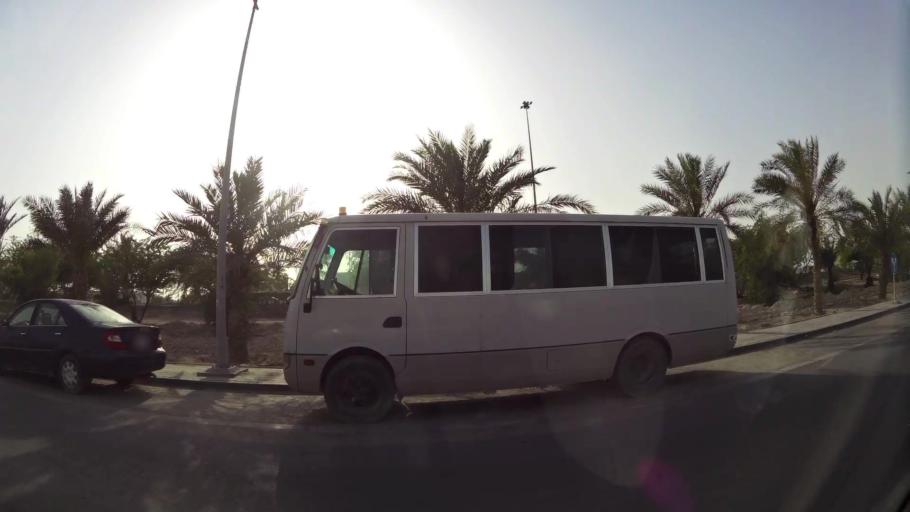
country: QA
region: Baladiyat ar Rayyan
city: Ar Rayyan
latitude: 25.2334
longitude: 51.4319
